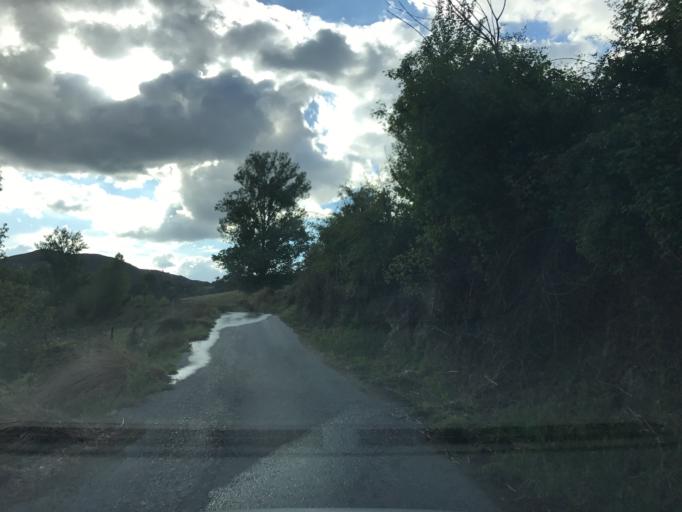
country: ES
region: Andalusia
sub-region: Provincia de Granada
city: Diezma
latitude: 37.2416
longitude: -3.3747
